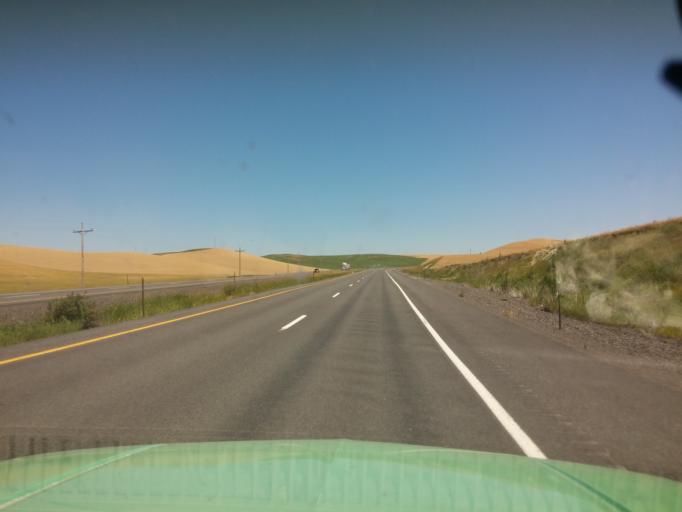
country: US
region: Idaho
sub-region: Nez Perce County
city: Lewiston
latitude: 46.5071
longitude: -116.9883
